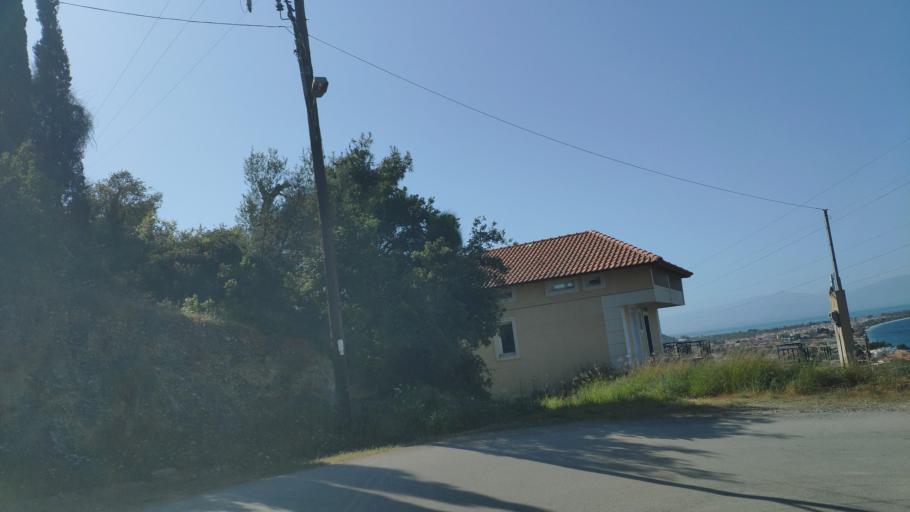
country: GR
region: West Greece
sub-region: Nomos Achaias
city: Aiyira
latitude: 38.1464
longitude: 22.3540
